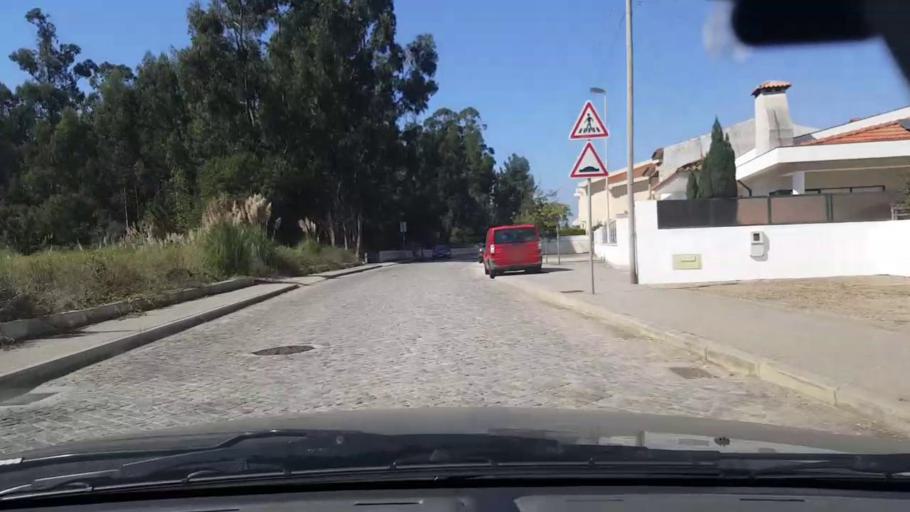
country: PT
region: Porto
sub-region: Vila do Conde
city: Arvore
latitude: 41.3044
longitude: -8.7149
